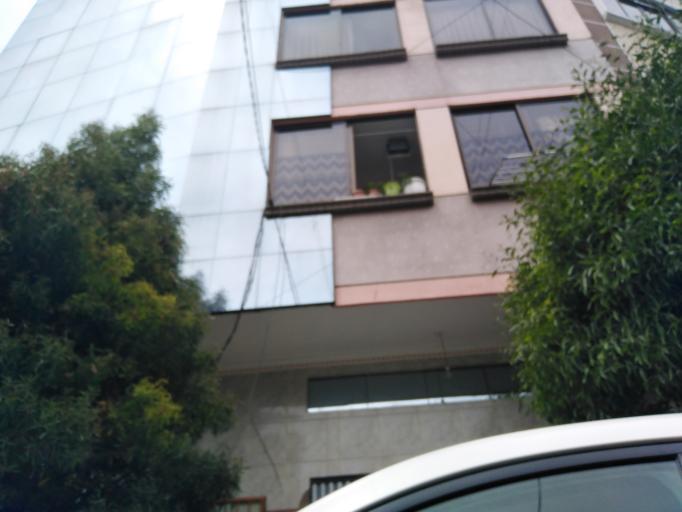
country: BO
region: La Paz
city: La Paz
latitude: -16.5131
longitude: -68.1361
